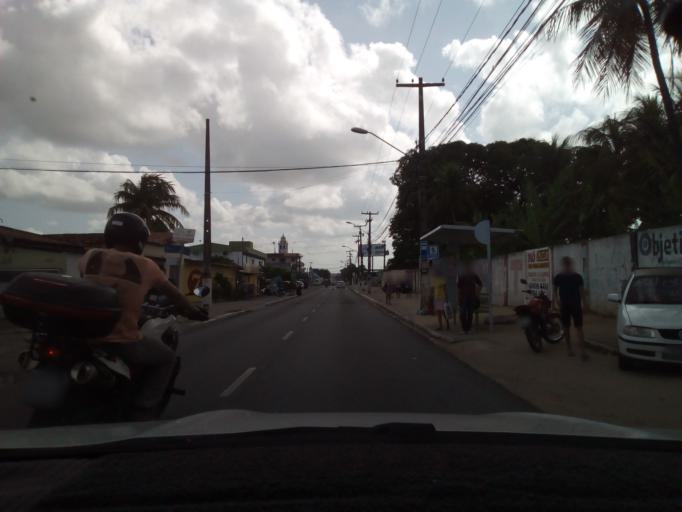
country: BR
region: Paraiba
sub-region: Bayeux
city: Bayeux
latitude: -7.1228
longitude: -34.9161
